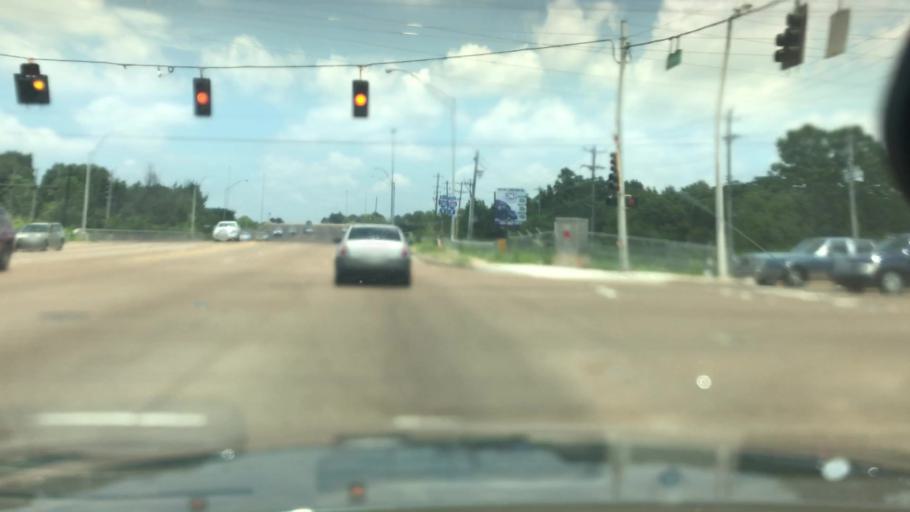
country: US
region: Mississippi
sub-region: De Soto County
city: Southaven
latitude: 35.0763
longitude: -89.9314
